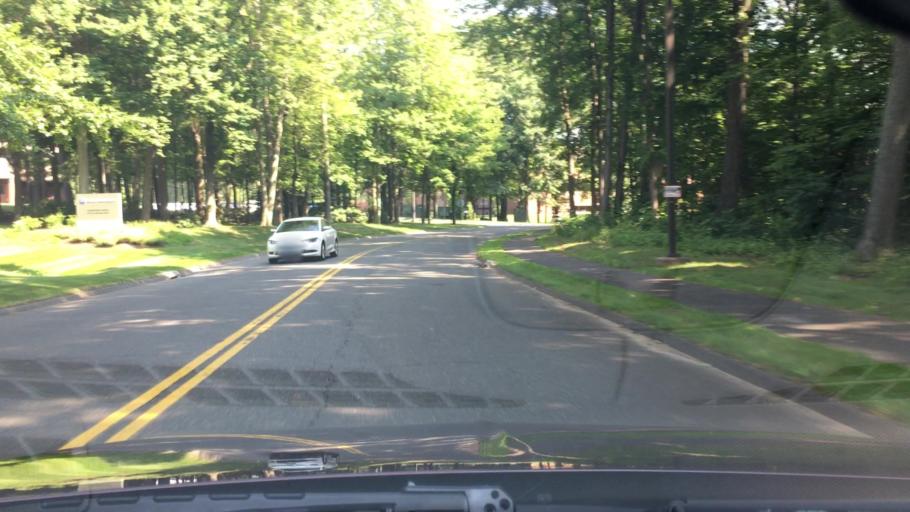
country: US
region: Connecticut
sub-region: Hartford County
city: Farmington
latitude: 41.7106
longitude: -72.8045
